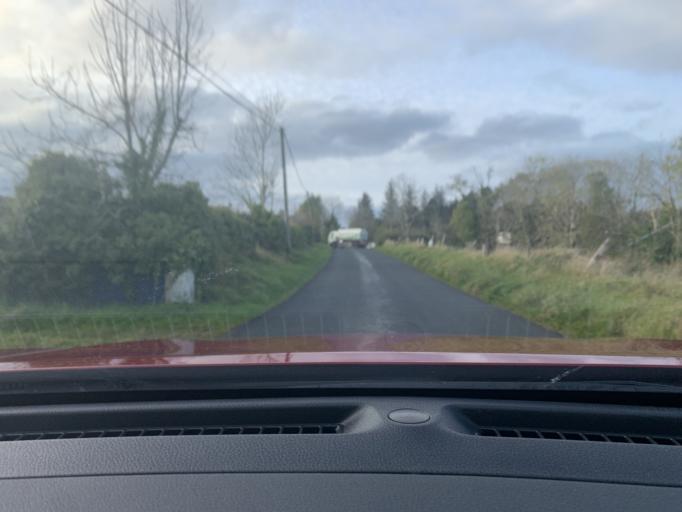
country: IE
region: Connaught
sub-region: Roscommon
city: Ballaghaderreen
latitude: 53.9106
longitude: -8.5828
